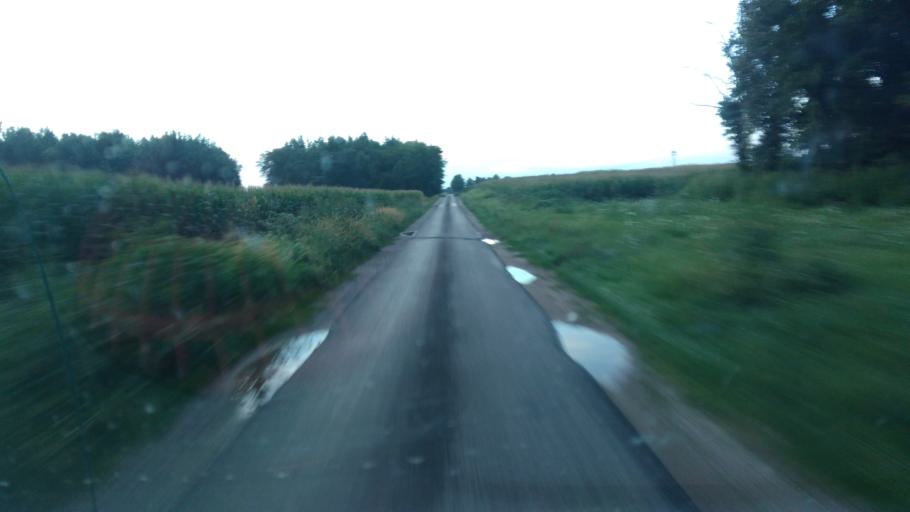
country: US
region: Ohio
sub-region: Crawford County
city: Galion
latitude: 40.7058
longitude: -82.8655
